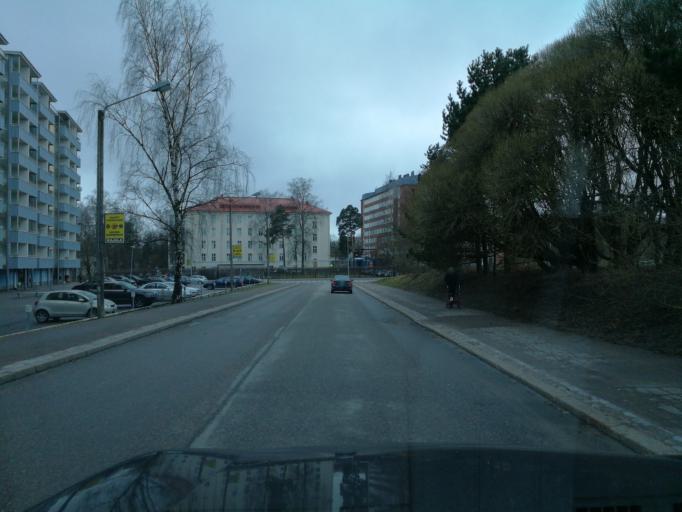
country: FI
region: Uusimaa
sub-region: Helsinki
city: Helsinki
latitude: 60.2181
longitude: 24.9658
